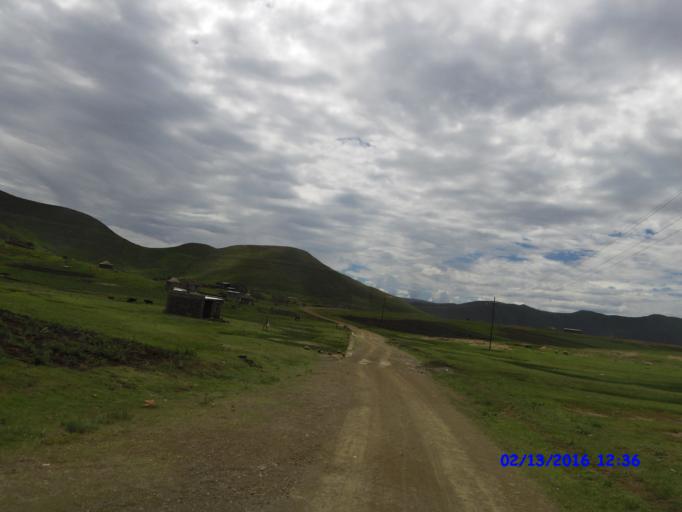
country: LS
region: Maseru
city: Nako
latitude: -29.8398
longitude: 28.0244
